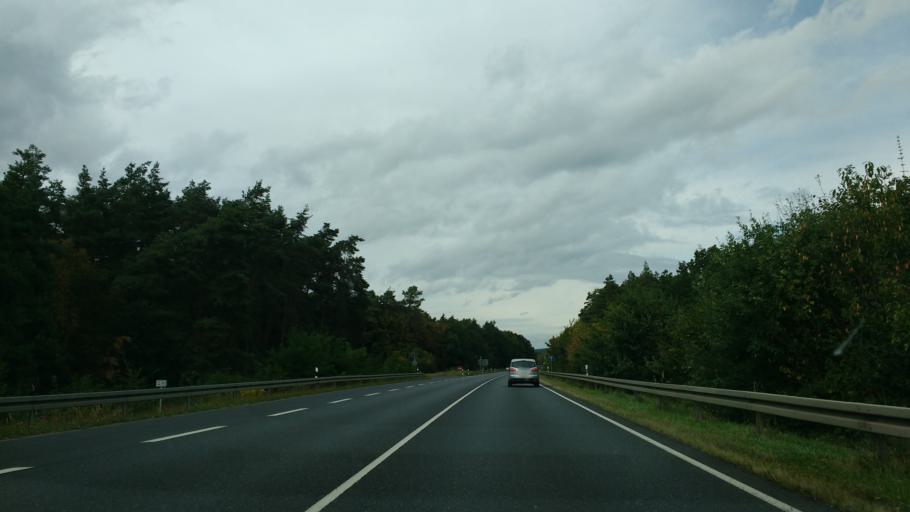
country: DE
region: Bavaria
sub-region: Regierungsbezirk Unterfranken
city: Schwebheim
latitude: 50.0153
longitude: 10.2379
